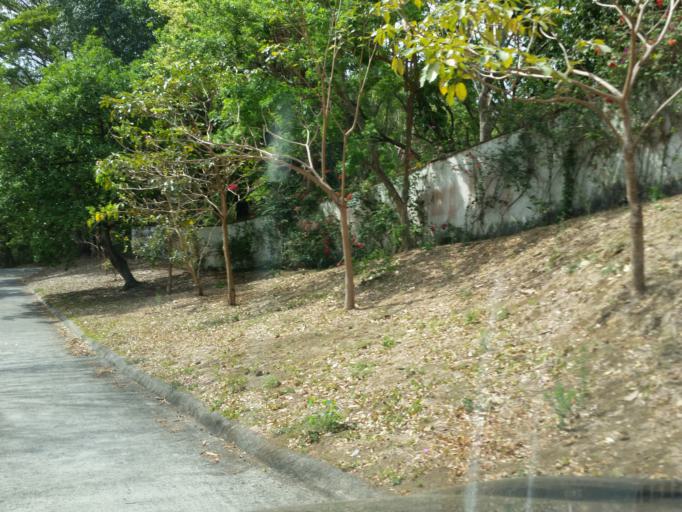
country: NI
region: Masaya
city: Ticuantepe
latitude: 12.0510
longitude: -86.2570
